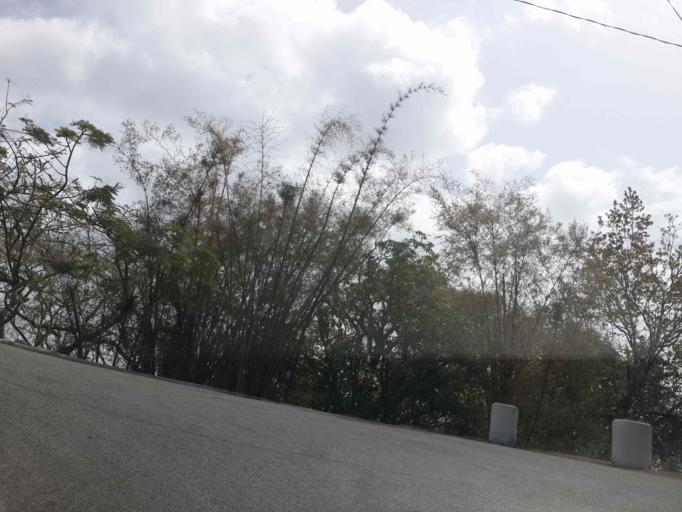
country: LC
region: Castries Quarter
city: Castries
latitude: 14.0065
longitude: -60.9982
